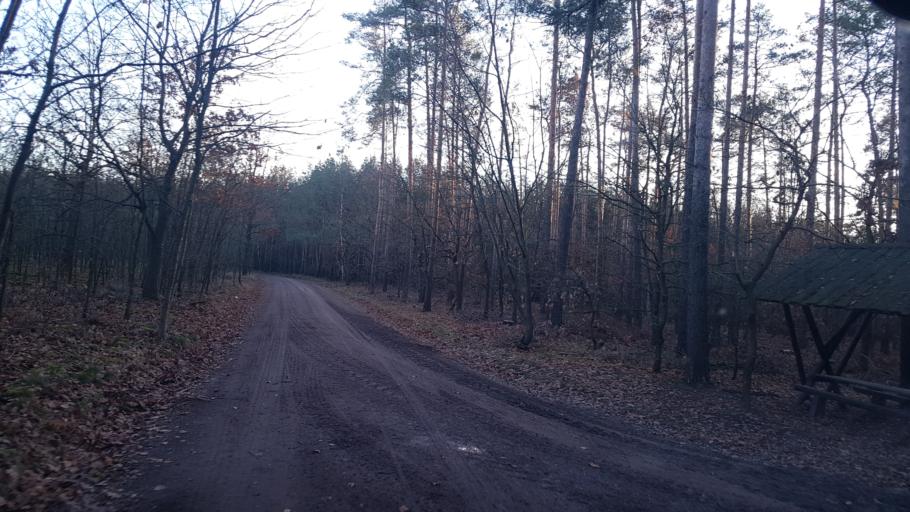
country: DE
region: Brandenburg
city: Falkenberg
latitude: 51.6265
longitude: 13.2778
